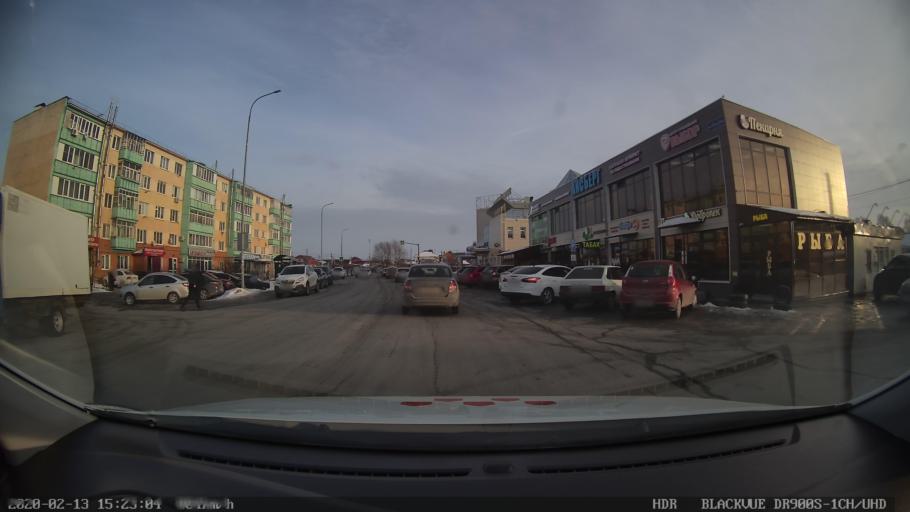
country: RU
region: Tatarstan
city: Vysokaya Gora
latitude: 55.9196
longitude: 49.3119
